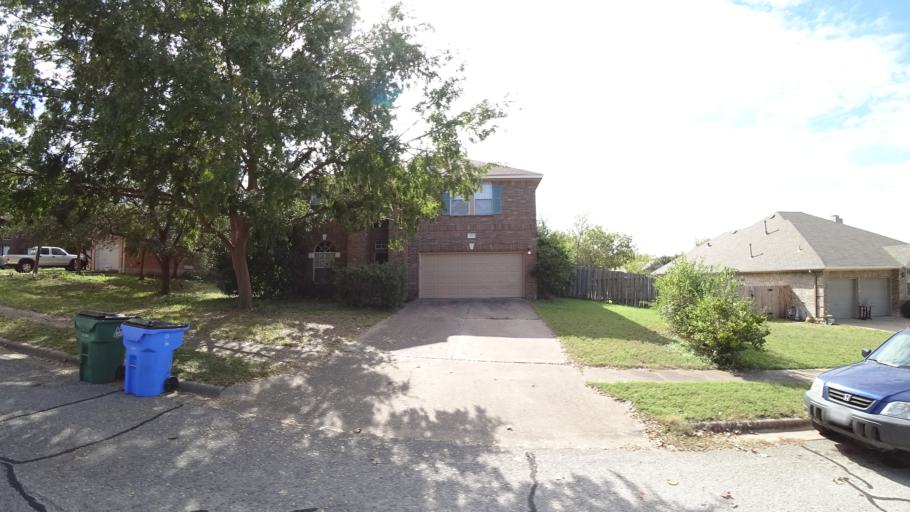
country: US
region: Texas
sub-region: Travis County
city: Pflugerville
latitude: 30.4444
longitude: -97.6251
